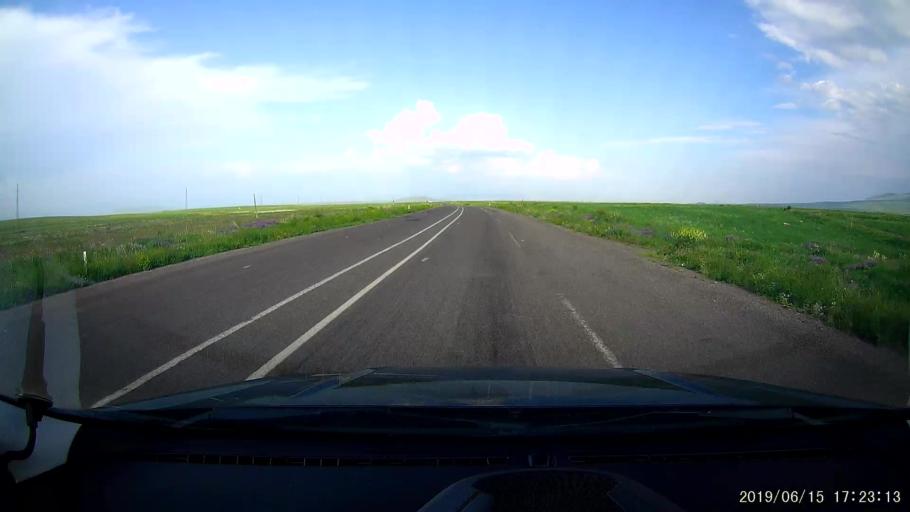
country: TR
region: Kars
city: Basgedikler
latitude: 40.6172
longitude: 43.3577
